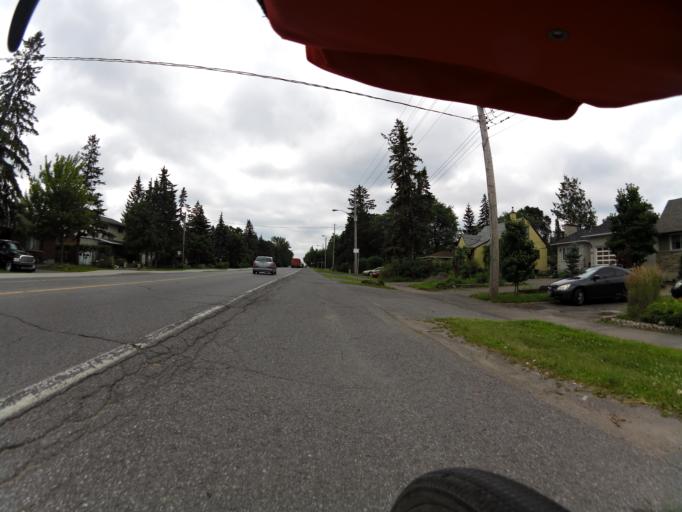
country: CA
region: Ontario
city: Ottawa
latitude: 45.3652
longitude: -75.7007
